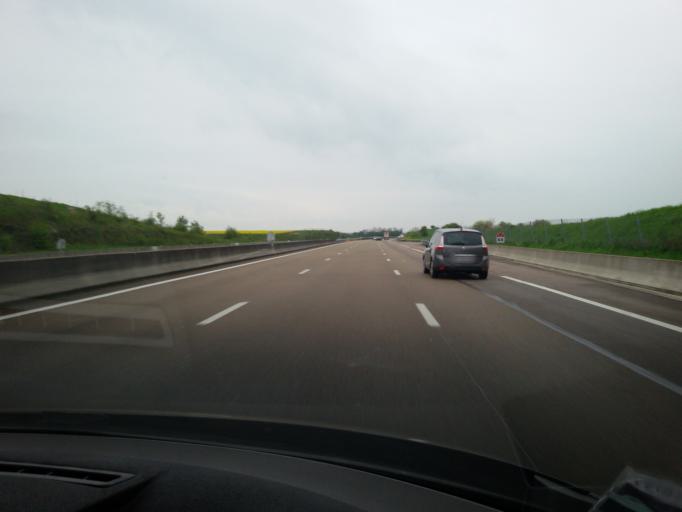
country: FR
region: Bourgogne
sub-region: Departement de la Cote-d'Or
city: Marcilly-sur-Tille
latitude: 47.4857
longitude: 5.1891
